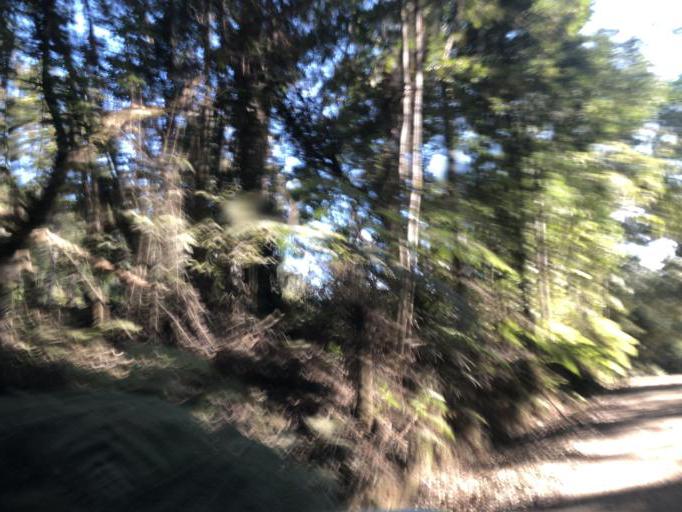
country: AU
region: New South Wales
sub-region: Bellingen
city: Bellingen
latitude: -30.4370
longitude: 152.8281
